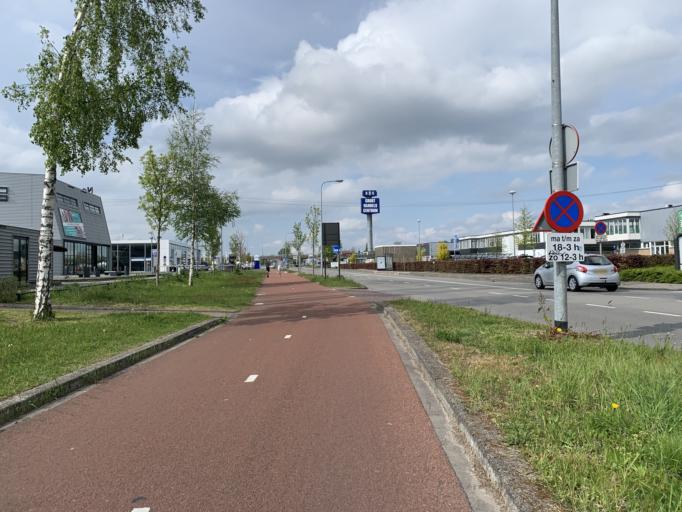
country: NL
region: Groningen
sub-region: Gemeente Groningen
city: Oosterpark
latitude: 53.2105
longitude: 6.5957
